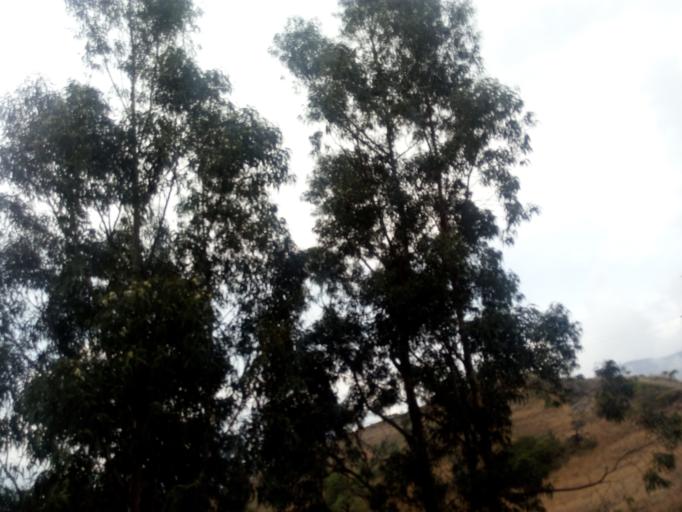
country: CO
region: Boyaca
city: Chita
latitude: 6.1918
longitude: -72.4931
